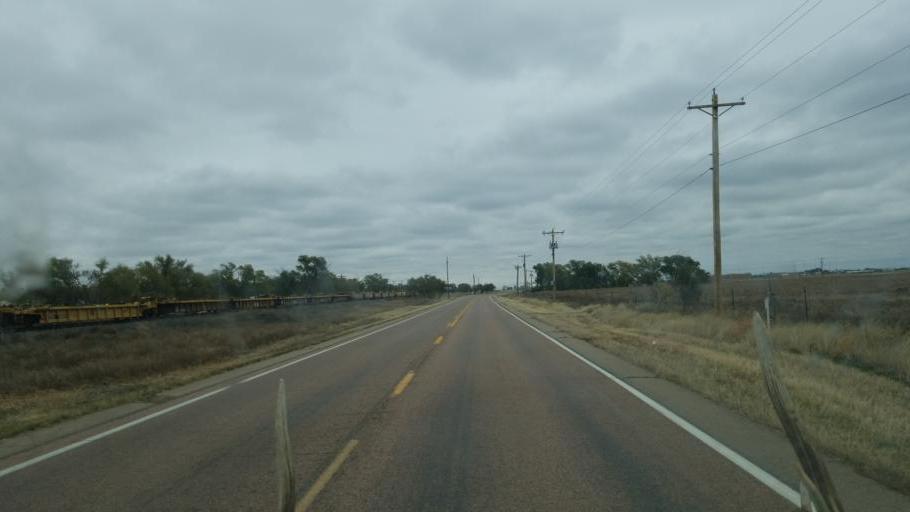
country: US
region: Colorado
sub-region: Crowley County
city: Ordway
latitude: 38.1905
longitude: -103.8619
